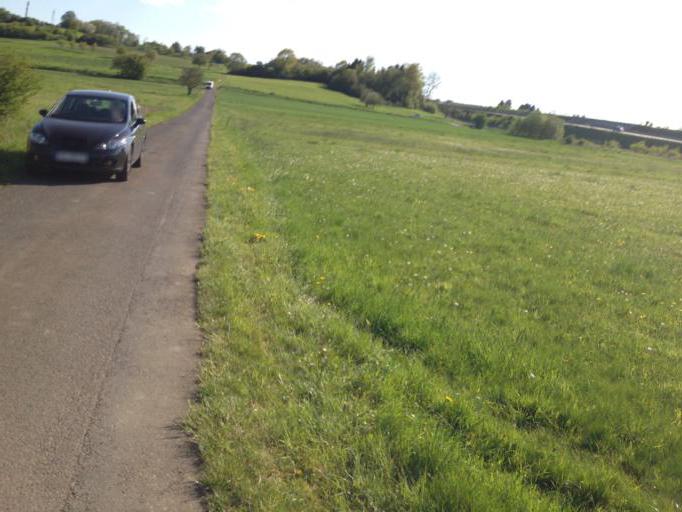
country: DE
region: Hesse
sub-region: Regierungsbezirk Giessen
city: Reiskirchen
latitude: 50.5842
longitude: 8.8101
